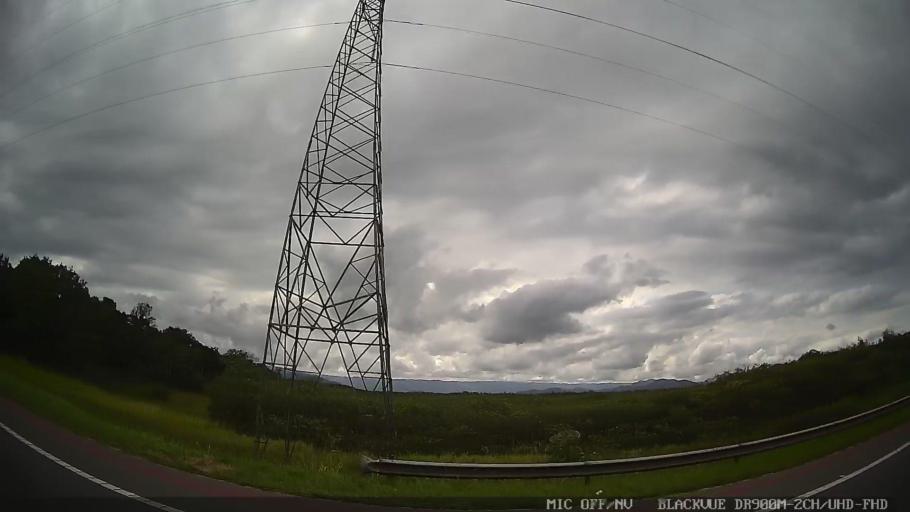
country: BR
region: Sao Paulo
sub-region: Itanhaem
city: Itanhaem
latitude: -24.1796
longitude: -46.8071
